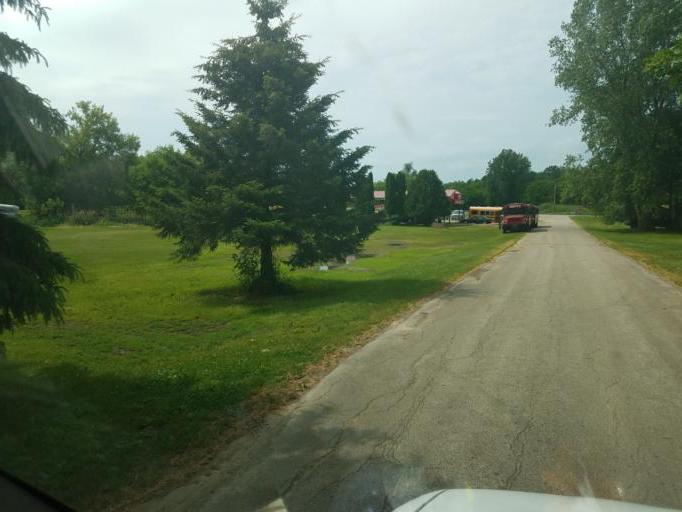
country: US
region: Wisconsin
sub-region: Monroe County
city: Cashton
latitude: 43.7230
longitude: -90.5882
